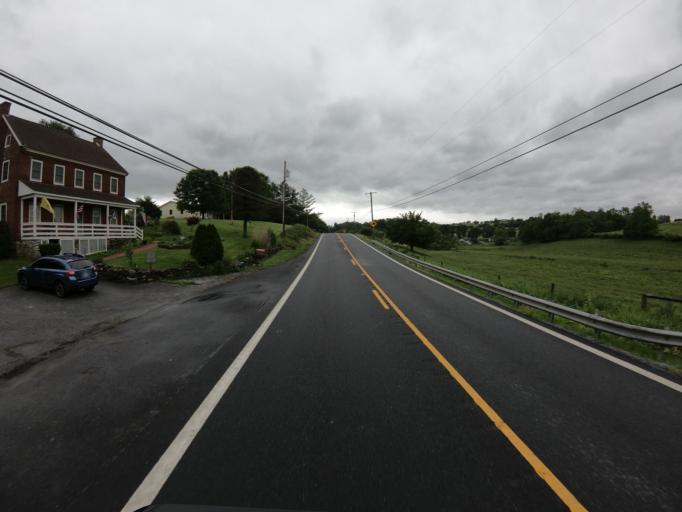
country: US
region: Maryland
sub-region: Frederick County
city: Myersville
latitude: 39.4683
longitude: -77.5949
